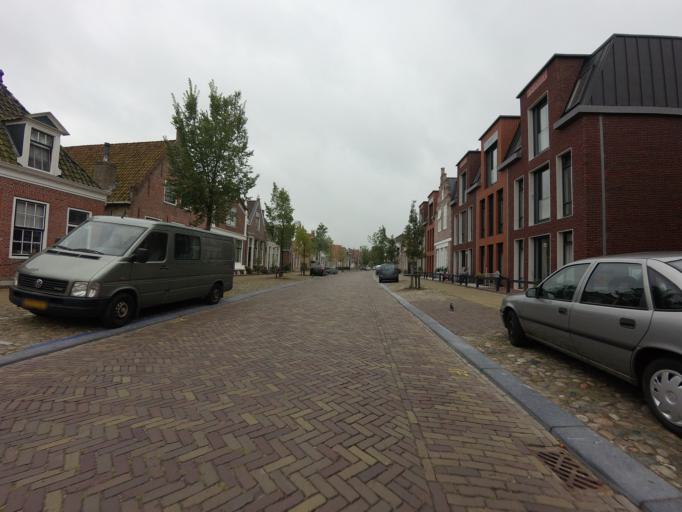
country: NL
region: Friesland
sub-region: Sudwest Fryslan
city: Workum
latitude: 52.9822
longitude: 5.4466
